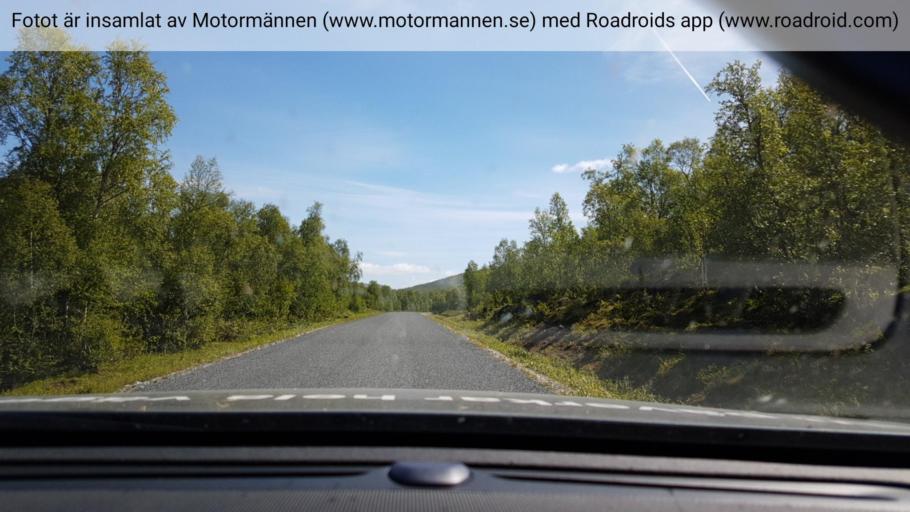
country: NO
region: Nordland
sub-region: Hattfjelldal
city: Hattfjelldal
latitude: 65.4212
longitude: 14.8433
